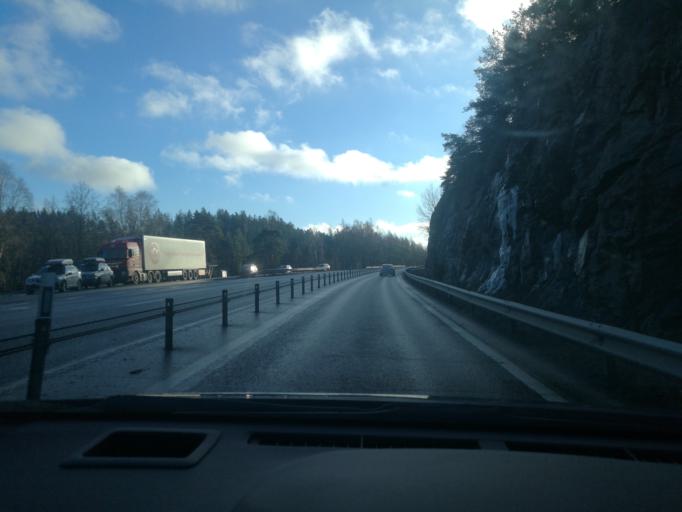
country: SE
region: OEstergoetland
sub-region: Norrkopings Kommun
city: Jursla
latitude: 58.7510
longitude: 16.1764
